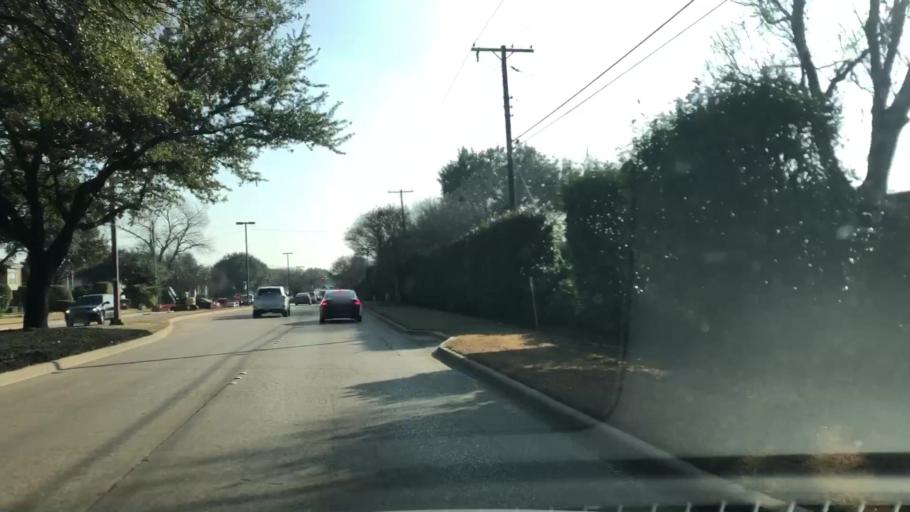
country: US
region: Texas
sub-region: Dallas County
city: Addison
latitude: 32.9436
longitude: -96.8558
